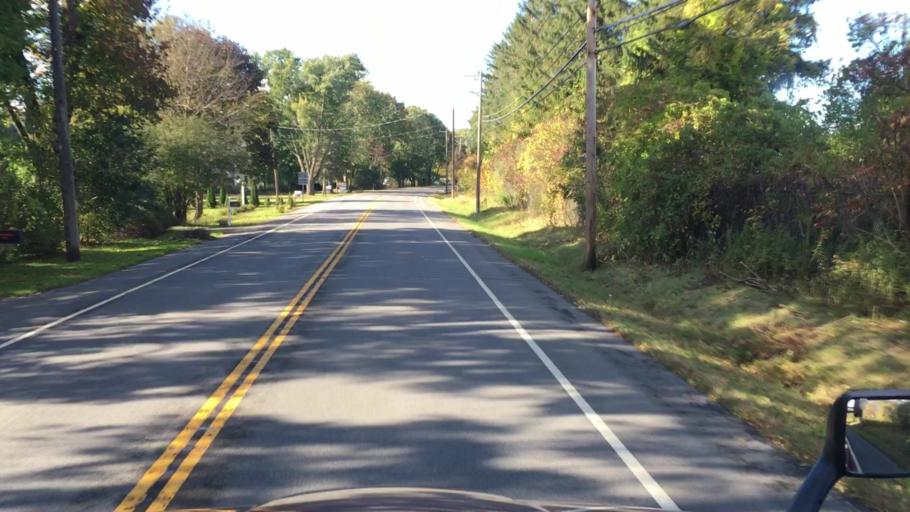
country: US
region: New York
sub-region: Schenectady County
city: Scotia
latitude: 42.8414
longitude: -73.9947
